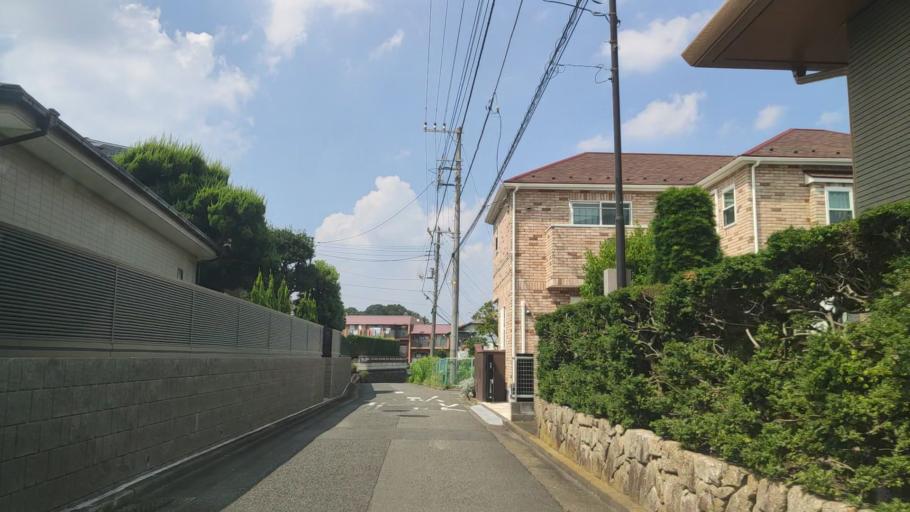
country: JP
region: Tokyo
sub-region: Machida-shi
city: Machida
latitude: 35.5425
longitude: 139.4377
